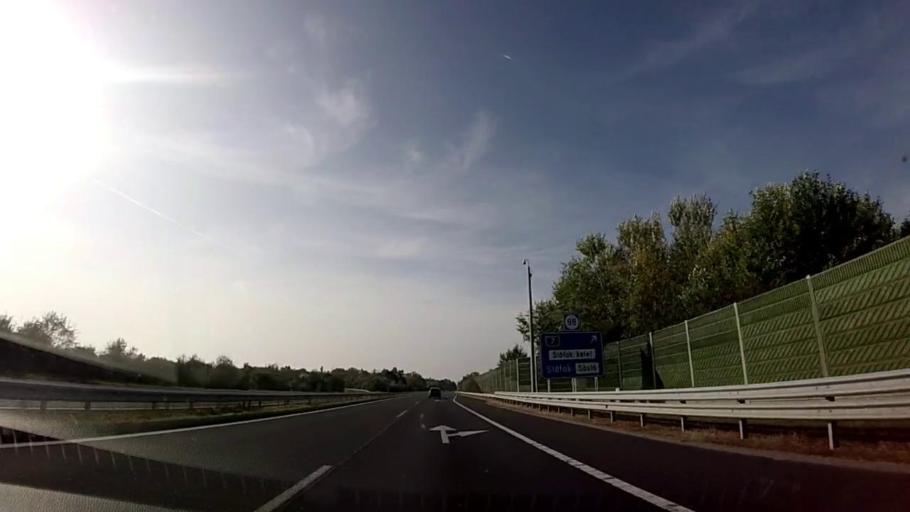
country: HU
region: Somogy
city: Balatonszabadi
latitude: 46.9368
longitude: 18.1431
